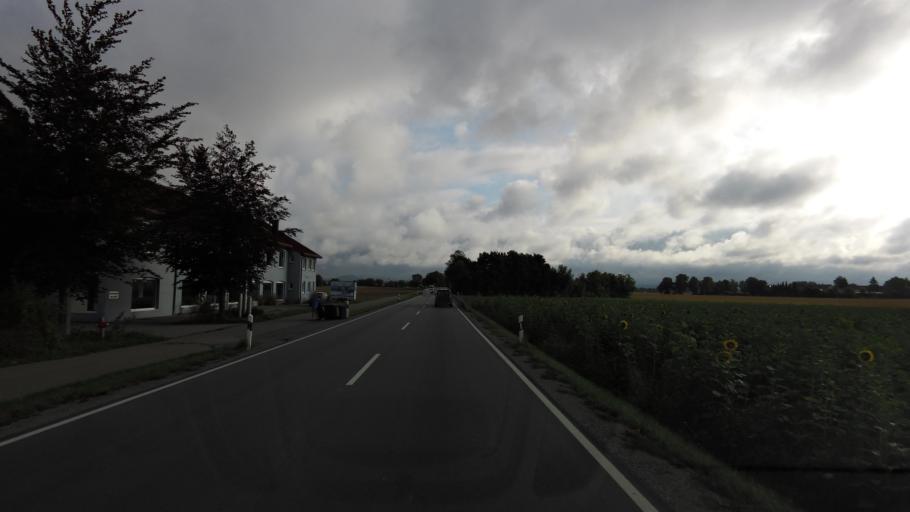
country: DE
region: Bavaria
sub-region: Lower Bavaria
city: Parkstetten
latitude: 48.9030
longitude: 12.5880
